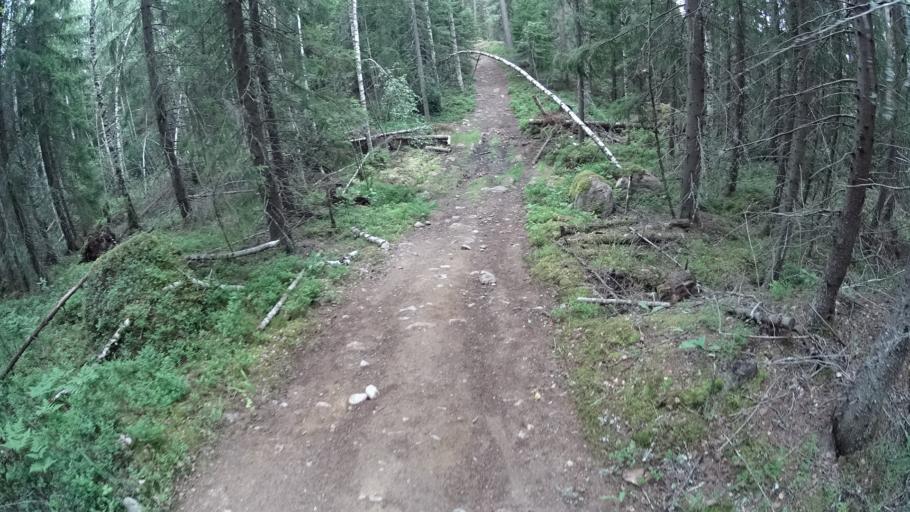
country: FI
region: Southern Savonia
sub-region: Mikkeli
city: Maentyharju
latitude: 61.1814
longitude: 26.8890
